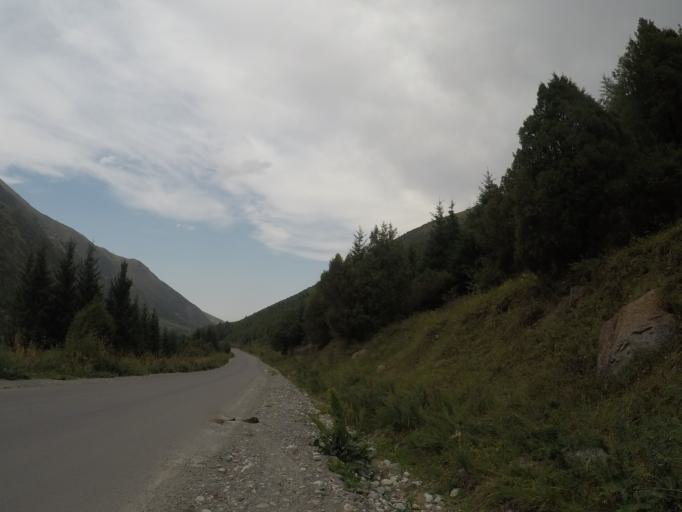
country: KG
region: Chuy
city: Bishkek
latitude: 42.5853
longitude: 74.4839
